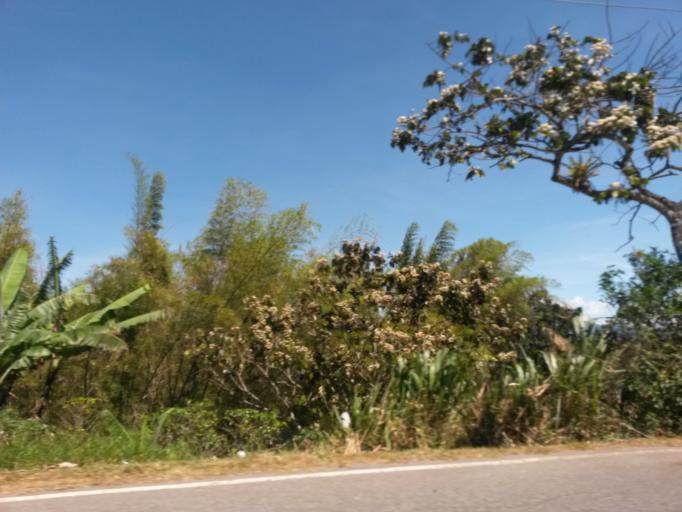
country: CO
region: Cauca
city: Lopez
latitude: 2.4425
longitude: -76.7916
